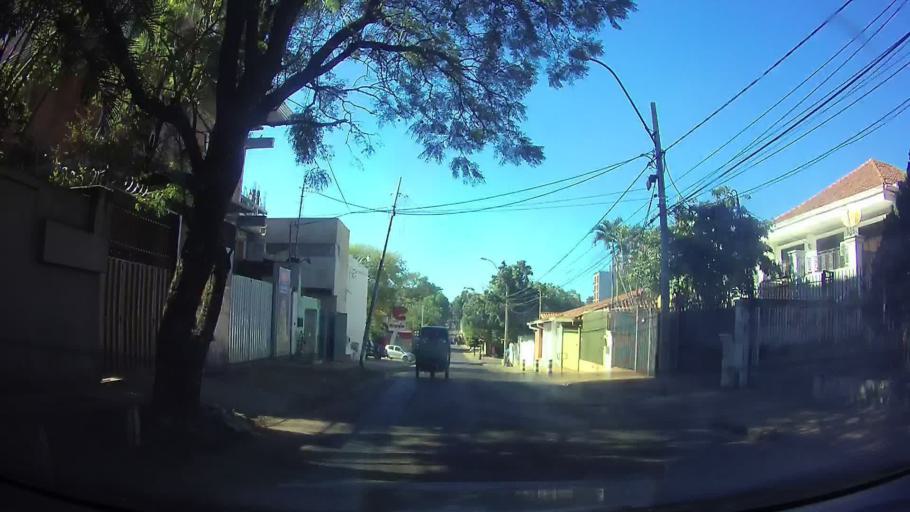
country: PY
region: Asuncion
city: Asuncion
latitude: -25.2970
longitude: -57.5870
